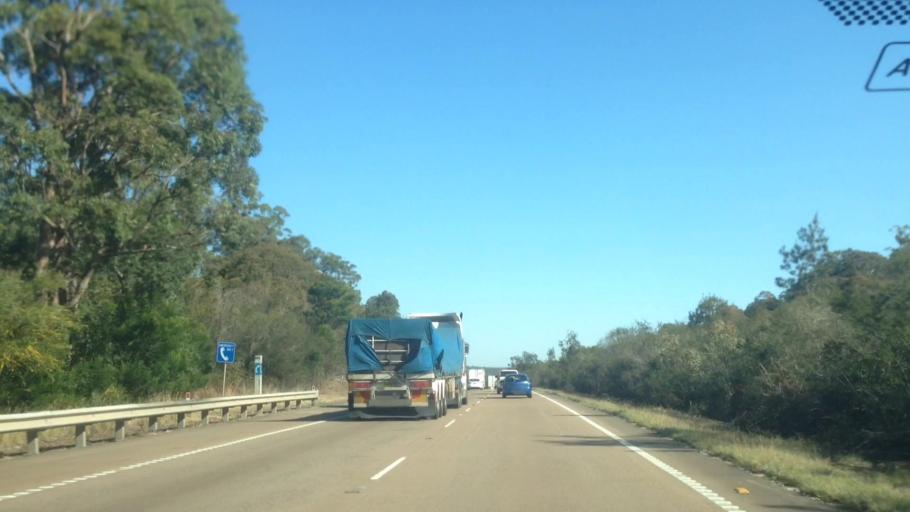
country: AU
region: New South Wales
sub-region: Lake Macquarie Shire
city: Dora Creek
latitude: -33.1496
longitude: 151.4736
